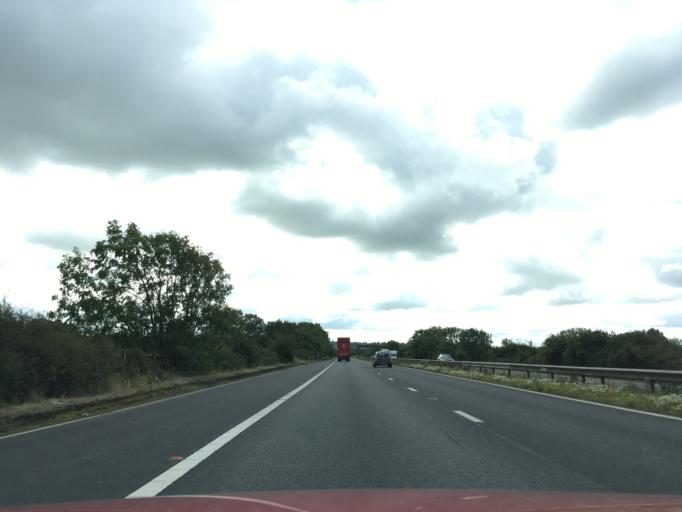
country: GB
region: England
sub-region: South Gloucestershire
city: Almondsbury
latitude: 51.5830
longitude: -2.5938
